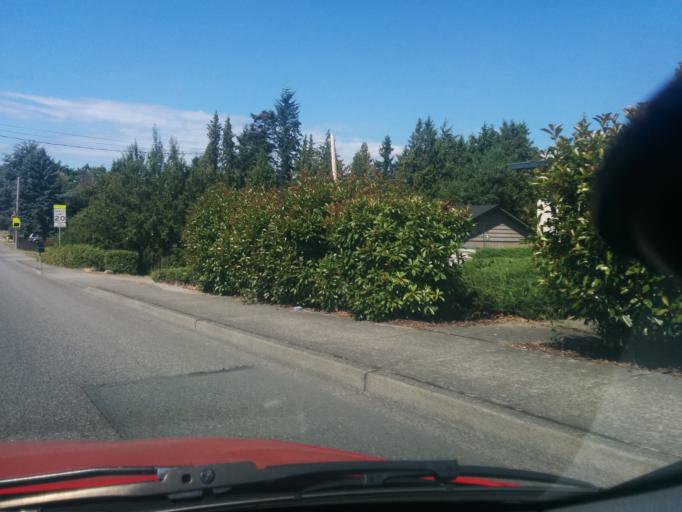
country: US
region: Washington
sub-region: Skagit County
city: Mount Vernon
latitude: 48.4285
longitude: -122.3246
